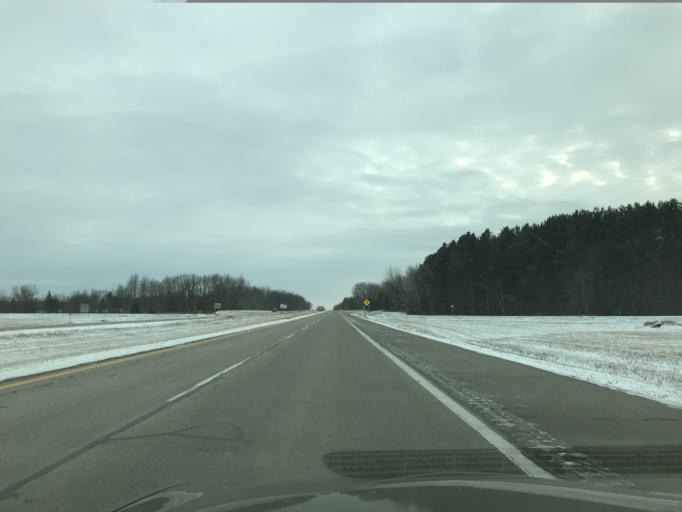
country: US
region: Michigan
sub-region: Roscommon County
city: Houghton Lake
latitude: 44.3347
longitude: -84.8072
